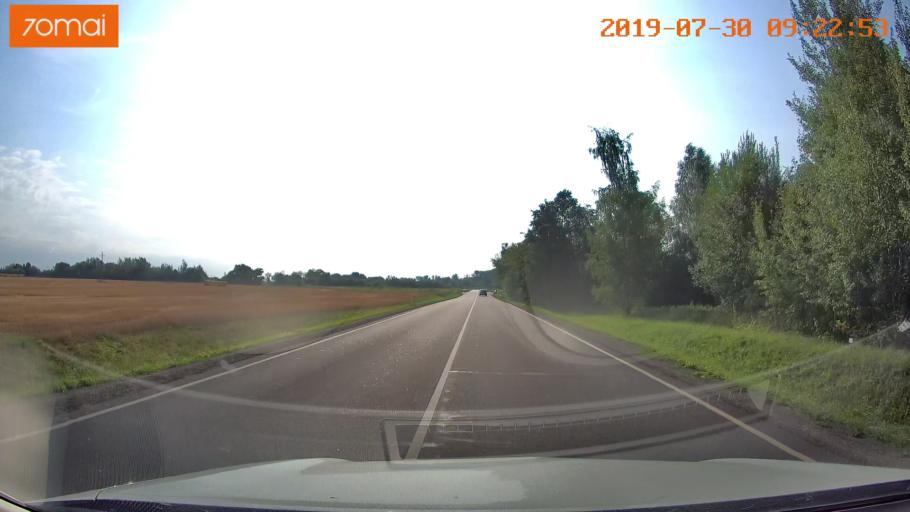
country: RU
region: Kaliningrad
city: Nesterov
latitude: 54.6335
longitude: 22.6640
